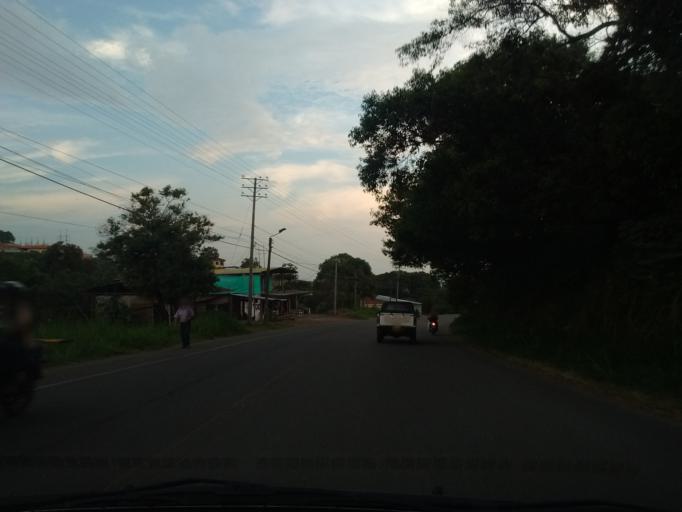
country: CO
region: Cauca
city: Santander de Quilichao
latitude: 3.0034
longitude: -76.4920
